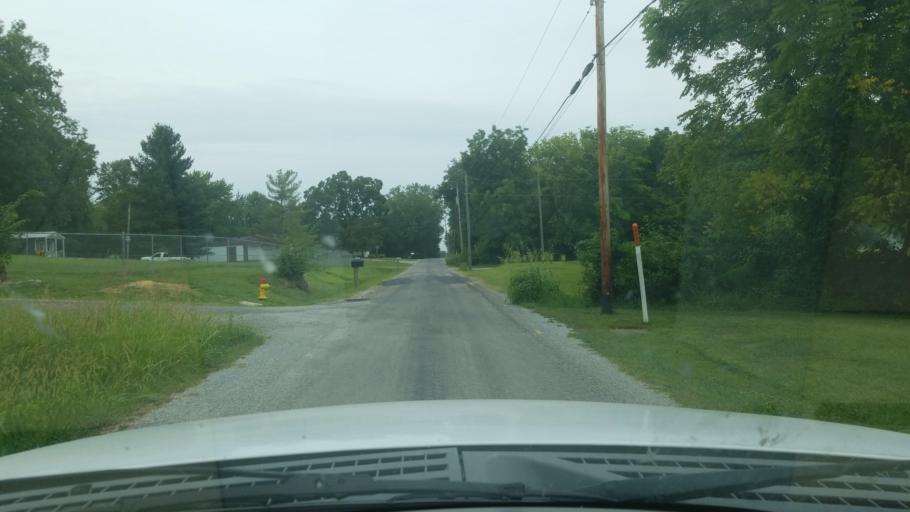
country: US
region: Illinois
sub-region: Saline County
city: Eldorado
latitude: 37.8235
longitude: -88.4477
